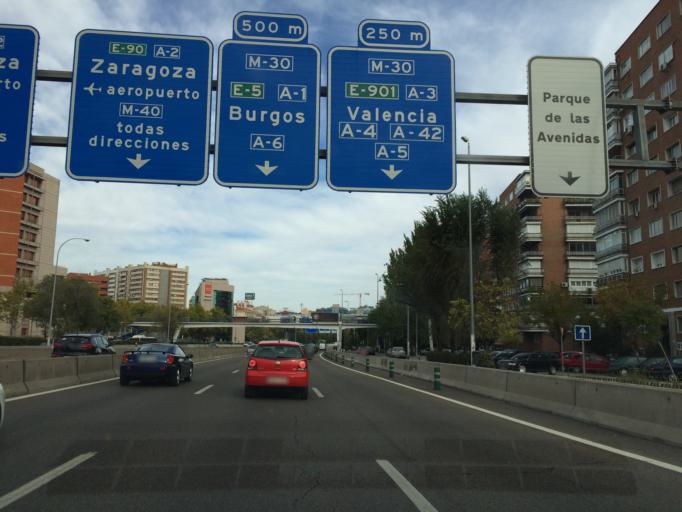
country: ES
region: Madrid
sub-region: Provincia de Madrid
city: Salamanca
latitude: 40.4421
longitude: -3.6663
